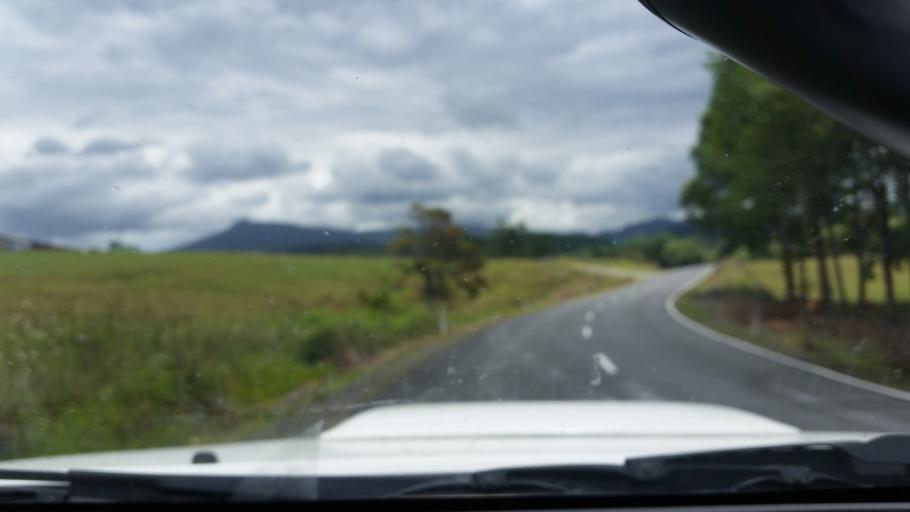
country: NZ
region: Northland
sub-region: Kaipara District
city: Dargaville
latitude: -35.7503
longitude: 173.8883
